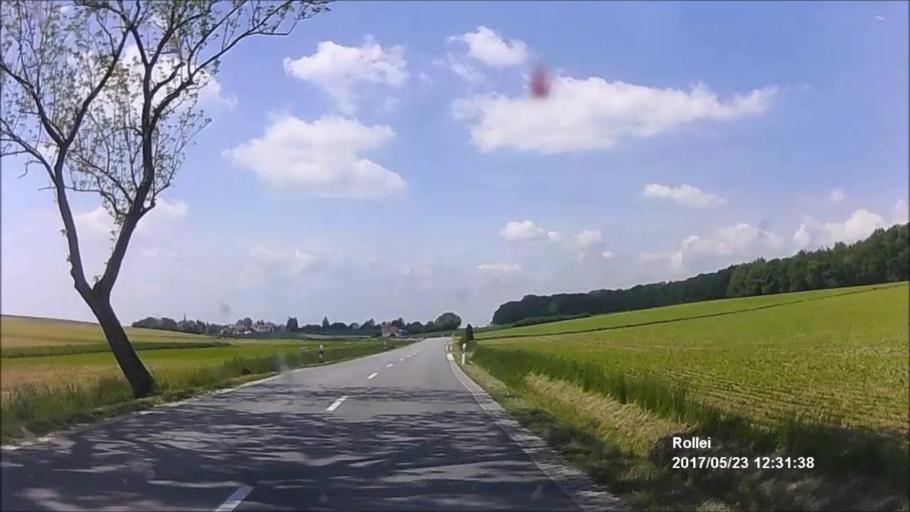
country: DE
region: Bavaria
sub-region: Lower Bavaria
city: Hohenthann
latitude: 48.6542
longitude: 12.1130
